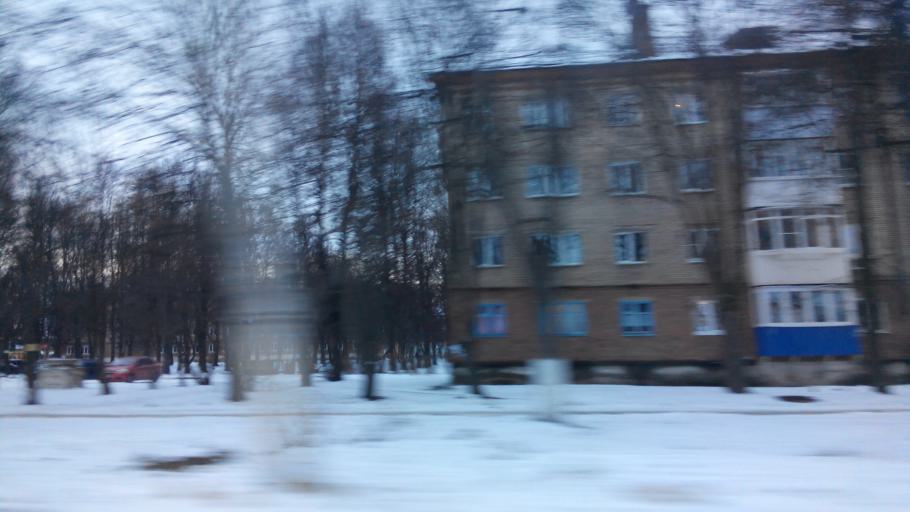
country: RU
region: Tula
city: Uzlovaya
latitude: 53.9802
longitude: 38.1907
